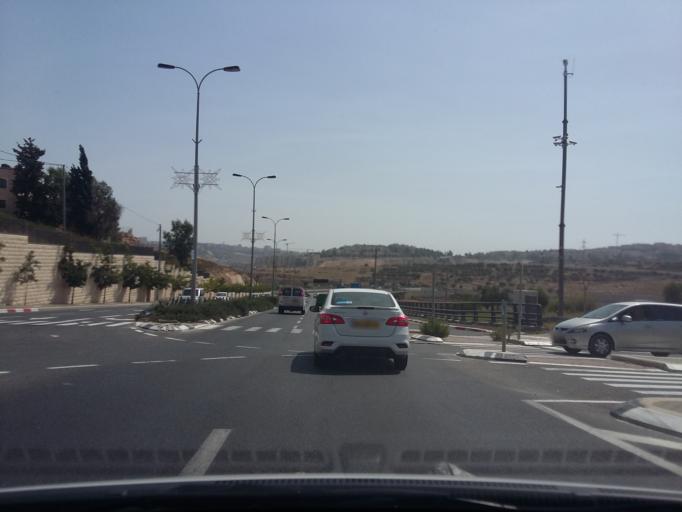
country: PS
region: West Bank
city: Ar Ram wa Dahiyat al Barid
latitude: 31.8288
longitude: 35.2188
